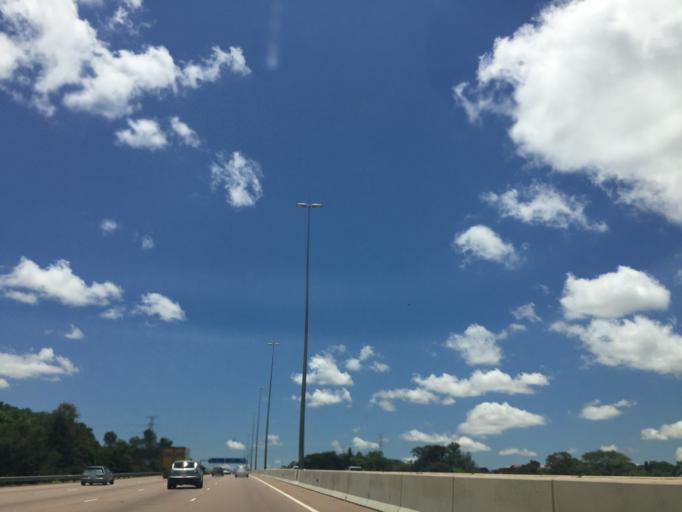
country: ZA
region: Gauteng
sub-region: City of Tshwane Metropolitan Municipality
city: Pretoria
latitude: -25.7298
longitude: 28.2650
